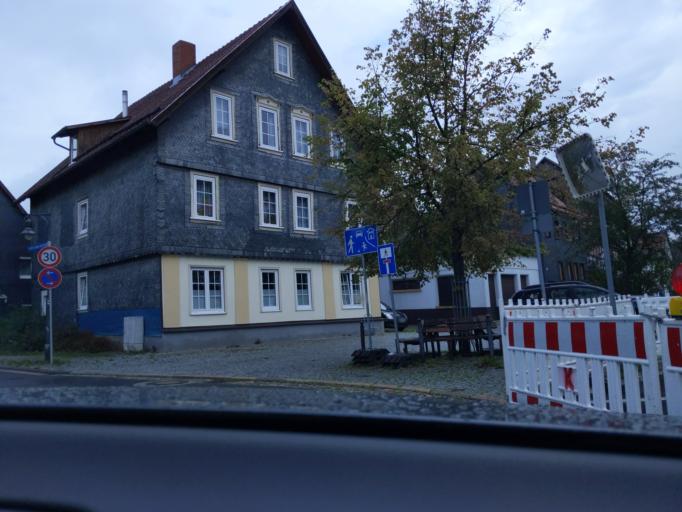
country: DE
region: Thuringia
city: Suhl
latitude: 50.5999
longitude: 10.6552
